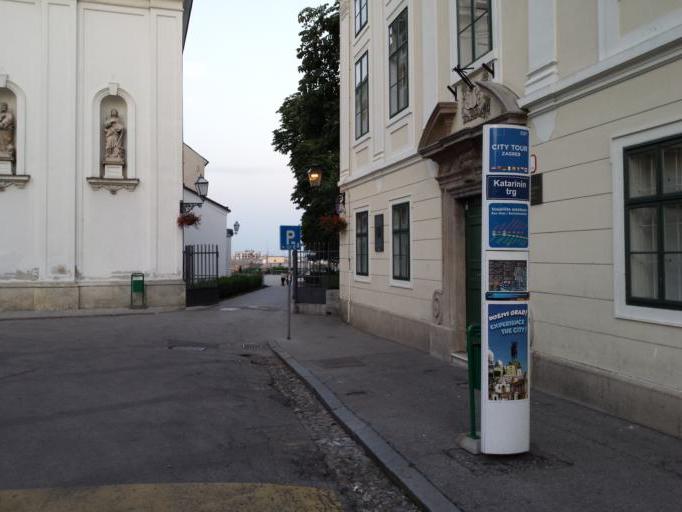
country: HR
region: Grad Zagreb
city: Zagreb - Centar
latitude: 45.8147
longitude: 15.9738
